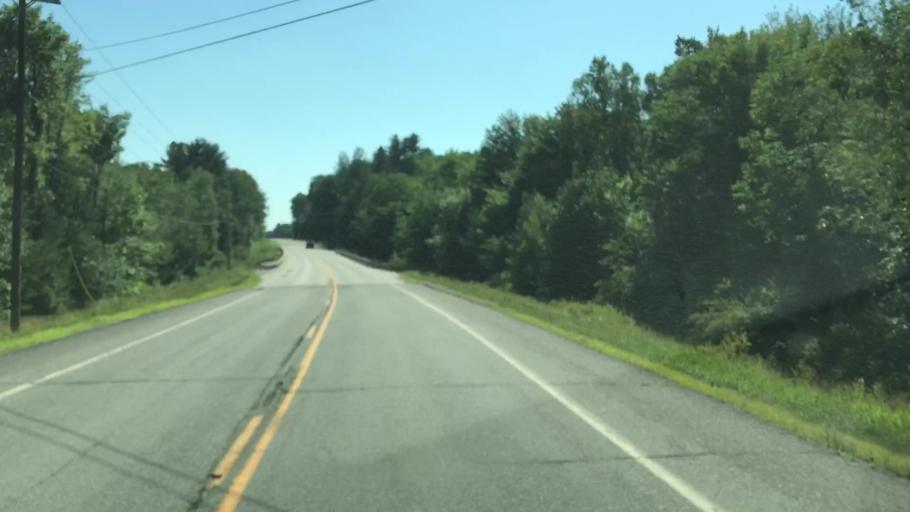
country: US
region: Maine
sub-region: Penobscot County
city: Lincoln
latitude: 45.3403
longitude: -68.5699
